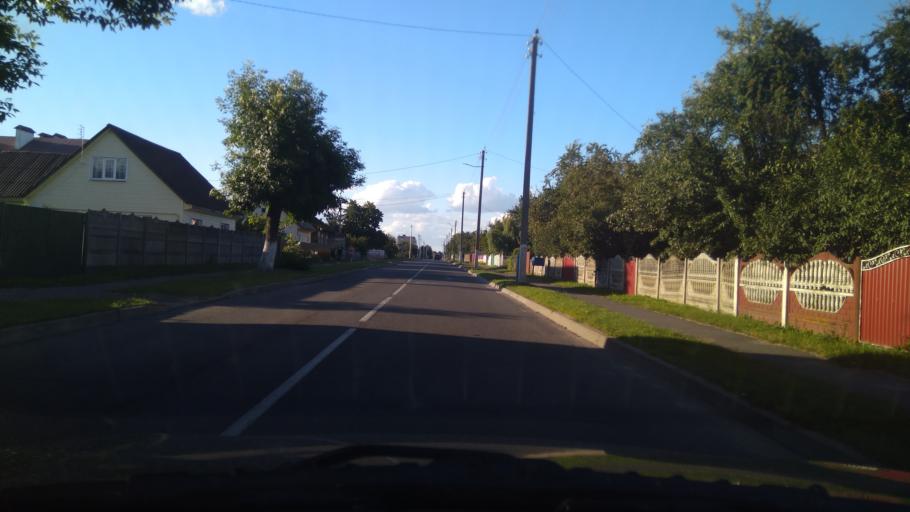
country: BY
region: Brest
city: Pruzhany
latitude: 52.5630
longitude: 24.4629
